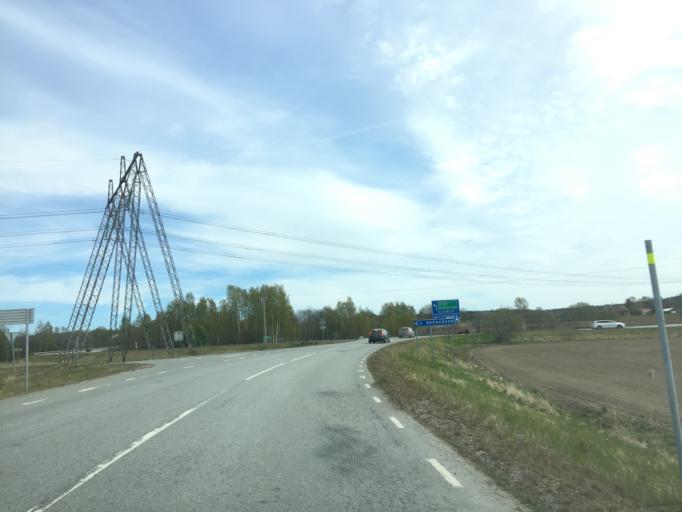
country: SE
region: OErebro
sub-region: Askersunds Kommun
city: Asbro
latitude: 59.0450
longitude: 14.9264
